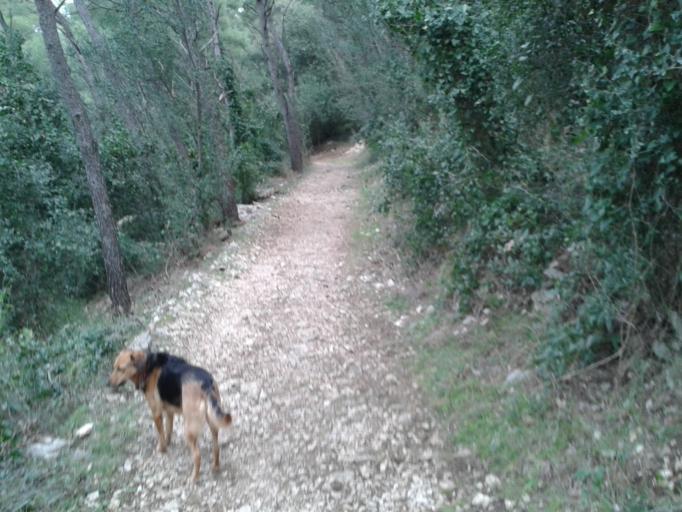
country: HR
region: Splitsko-Dalmatinska
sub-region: Grad Split
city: Split
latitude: 43.5105
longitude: 16.4003
